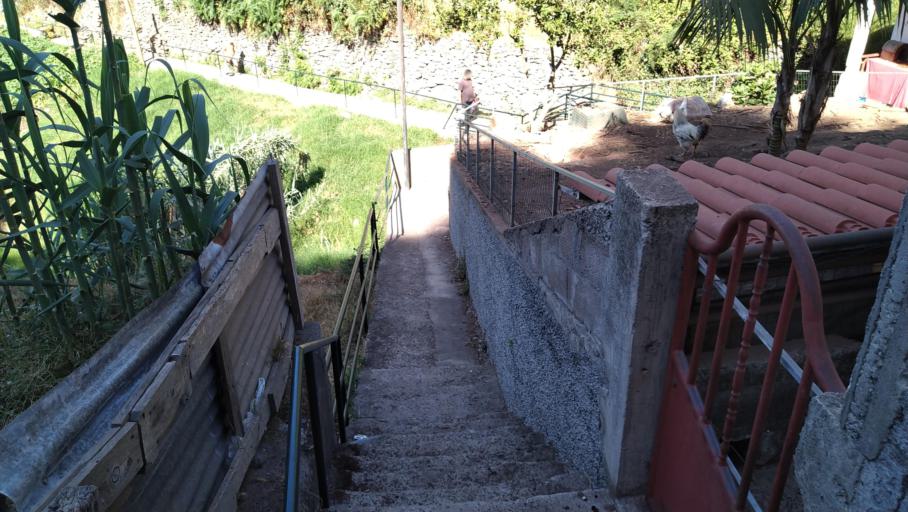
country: PT
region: Madeira
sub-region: Funchal
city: Nossa Senhora do Monte
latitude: 32.6807
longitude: -16.9402
